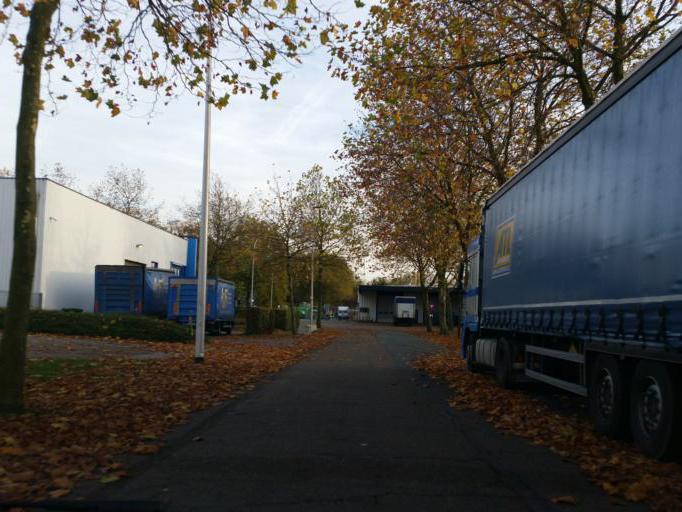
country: BE
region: Flanders
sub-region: Provincie Antwerpen
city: Hoboken
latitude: 51.1809
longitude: 4.3414
